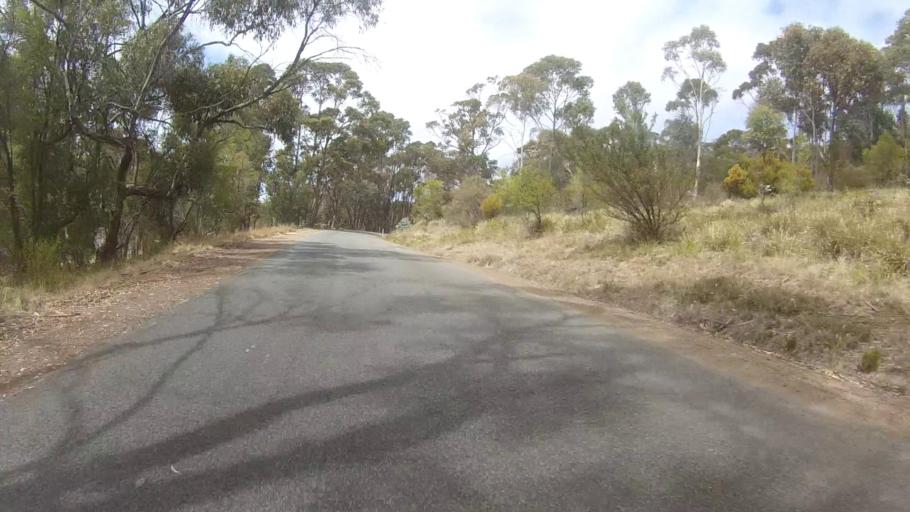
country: AU
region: Tasmania
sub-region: Kingborough
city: Blackmans Bay
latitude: -43.0470
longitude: 147.3385
